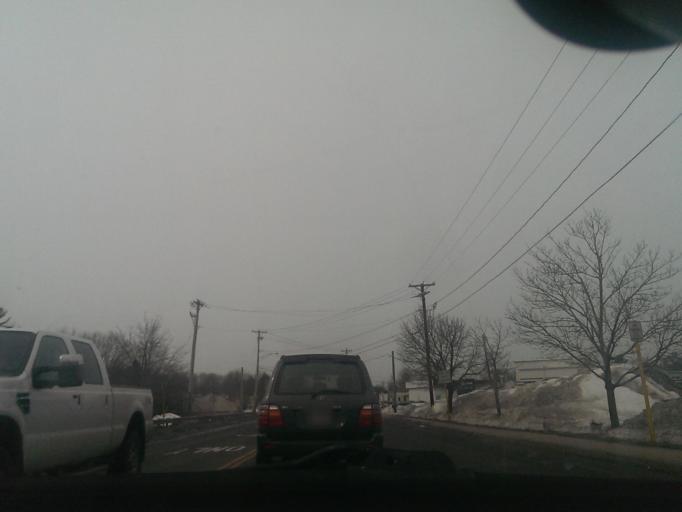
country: US
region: Massachusetts
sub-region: Hampden County
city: East Longmeadow
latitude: 42.0786
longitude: -72.5276
